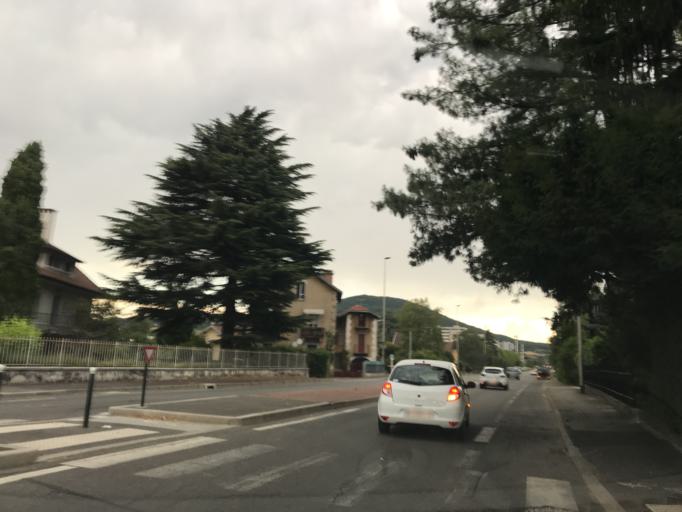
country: FR
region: Rhone-Alpes
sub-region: Departement de la Savoie
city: Tresserve
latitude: 45.6966
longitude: 5.9076
